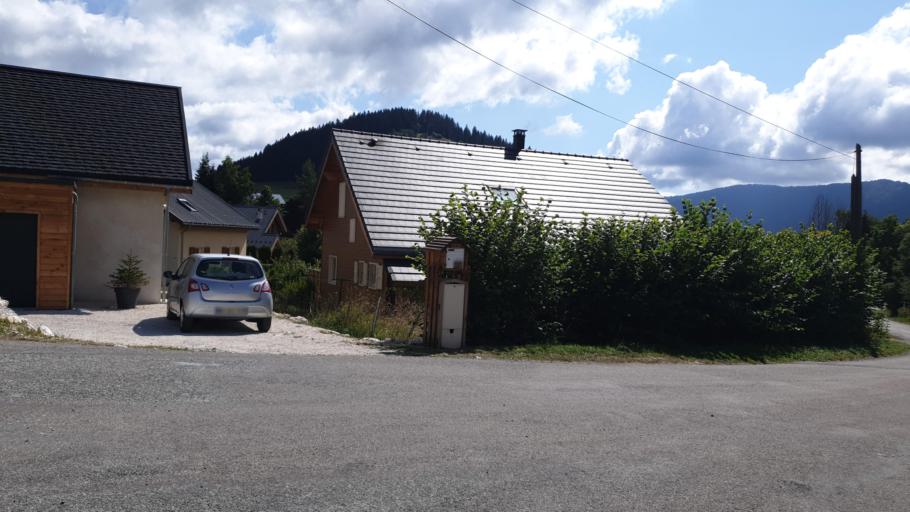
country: FR
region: Rhone-Alpes
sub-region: Departement de l'Isere
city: Autrans
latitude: 45.1758
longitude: 5.5503
